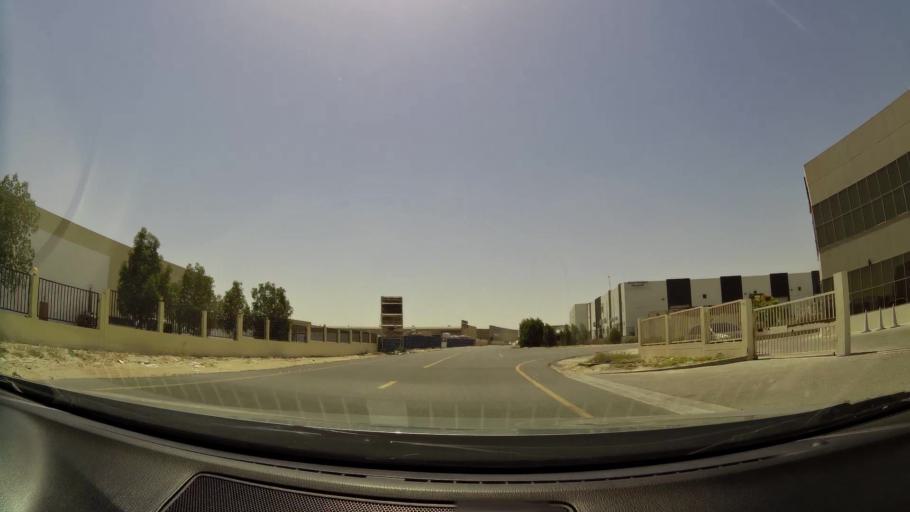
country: AE
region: Dubai
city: Dubai
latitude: 24.9832
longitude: 55.2090
